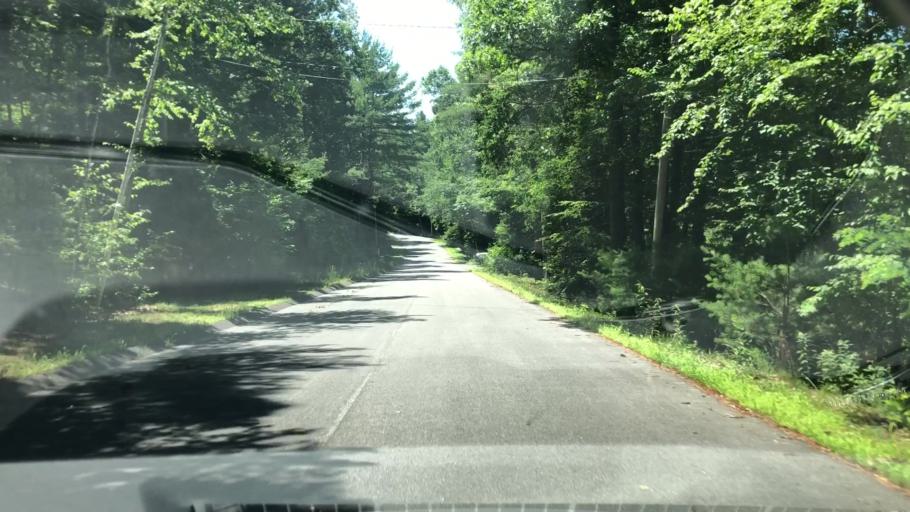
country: US
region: New Hampshire
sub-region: Hillsborough County
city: Milford
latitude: 42.8374
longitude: -71.5794
